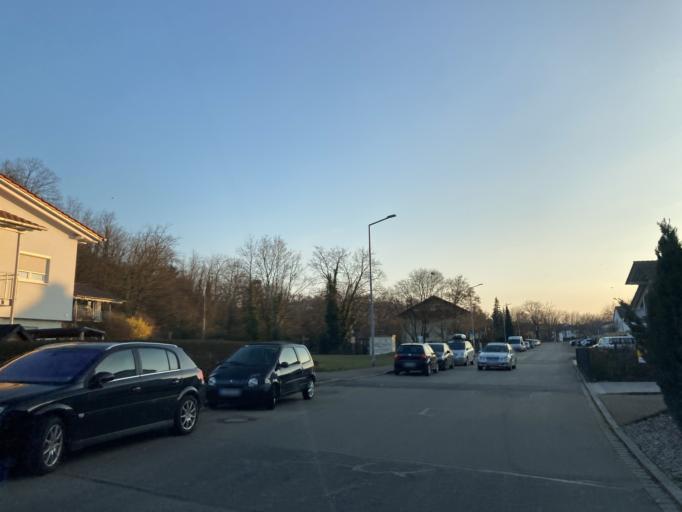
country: DE
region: Baden-Wuerttemberg
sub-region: Freiburg Region
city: Mullheim
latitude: 47.8136
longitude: 7.6133
